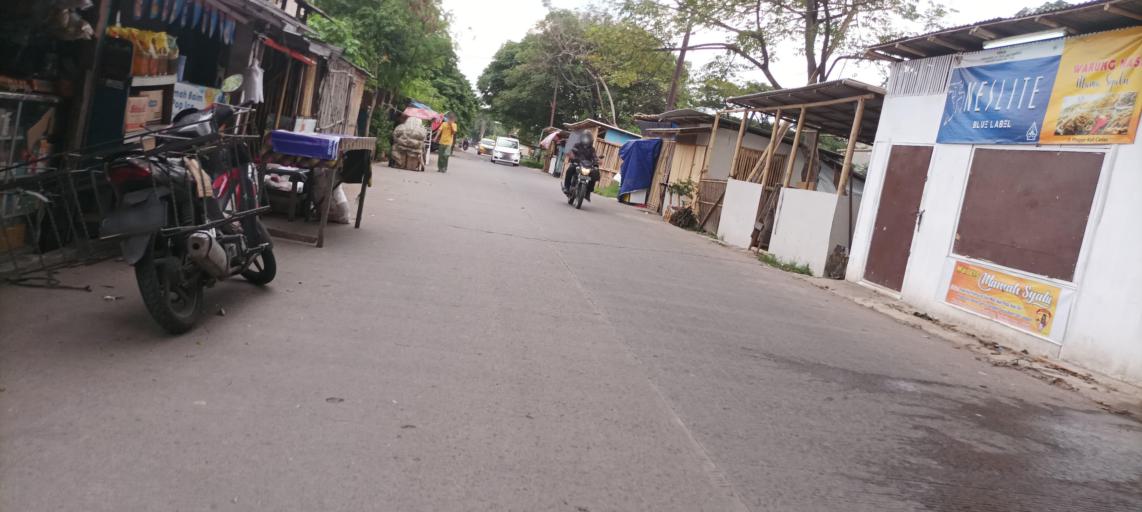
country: ID
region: West Java
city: Sepatan
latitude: -6.1400
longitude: 106.5878
